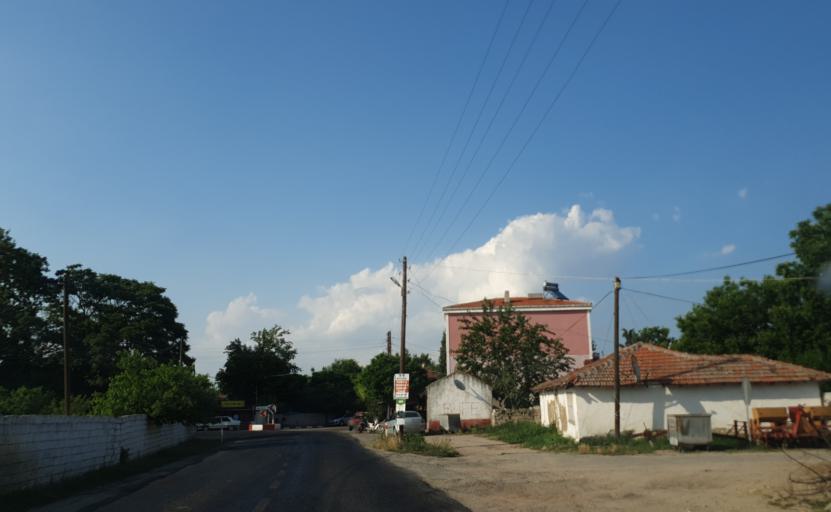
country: TR
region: Tekirdag
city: Muratli
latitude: 41.2014
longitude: 27.4712
